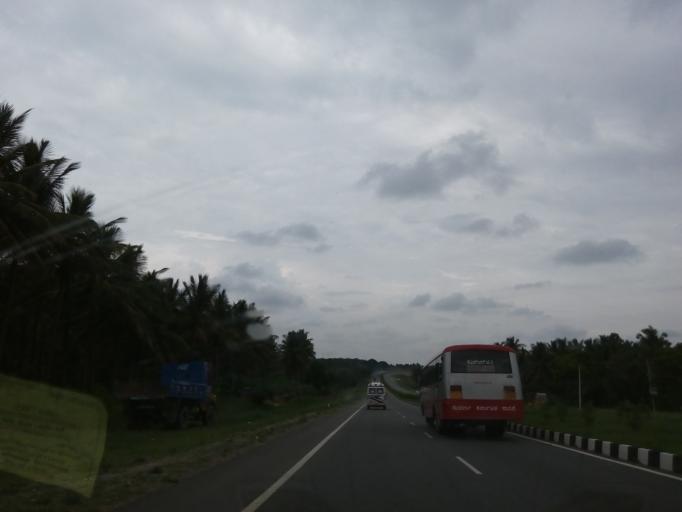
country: IN
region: Karnataka
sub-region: Hassan
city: Channarayapatna
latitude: 12.9418
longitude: 76.3466
